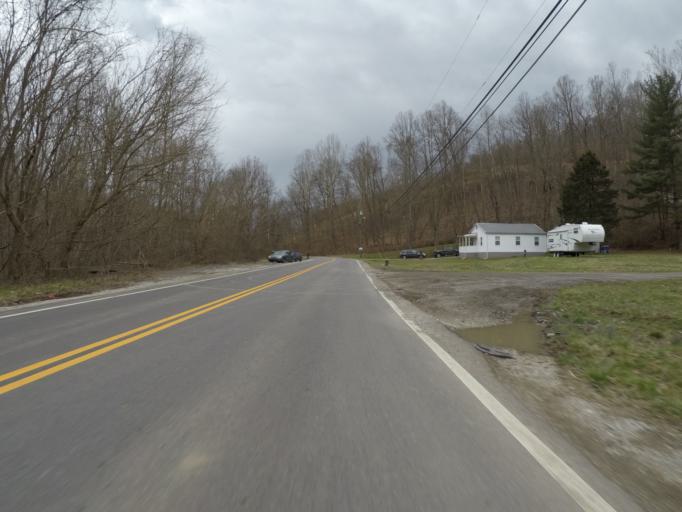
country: US
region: Ohio
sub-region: Lawrence County
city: Burlington
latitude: 38.4320
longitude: -82.4937
